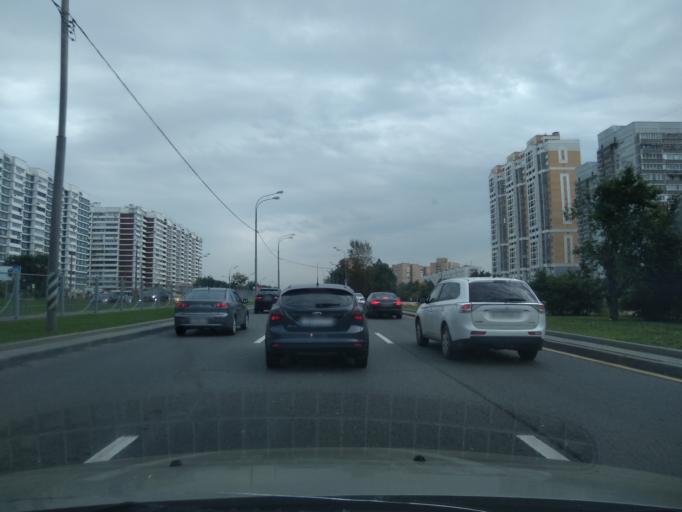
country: RU
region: Moskovskaya
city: Bol'shaya Setun'
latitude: 55.7406
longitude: 37.4310
